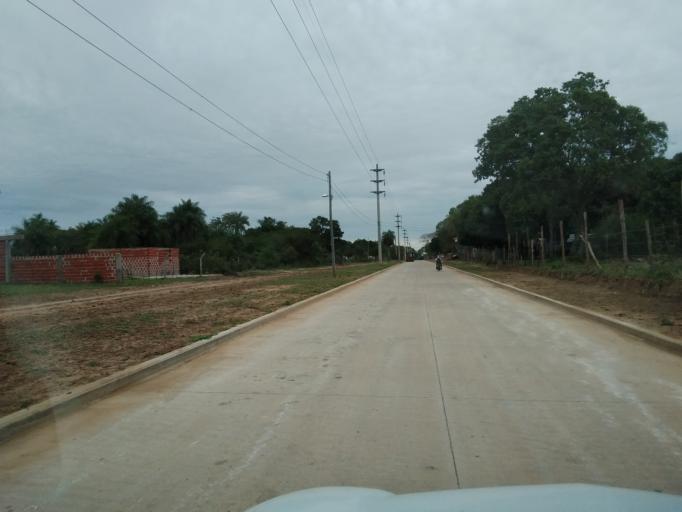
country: AR
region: Corrientes
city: Corrientes
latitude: -27.5122
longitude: -58.8218
